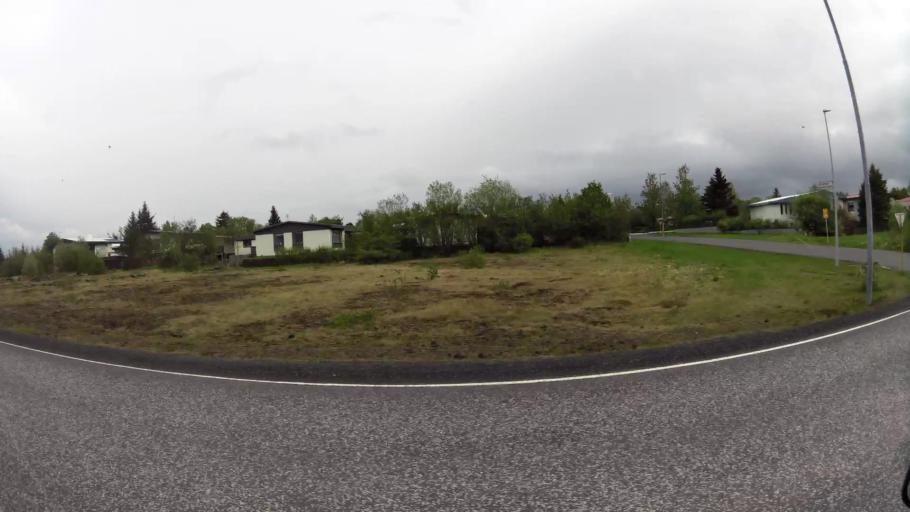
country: IS
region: Capital Region
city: Hafnarfjoerdur
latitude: 64.0824
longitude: -21.9691
